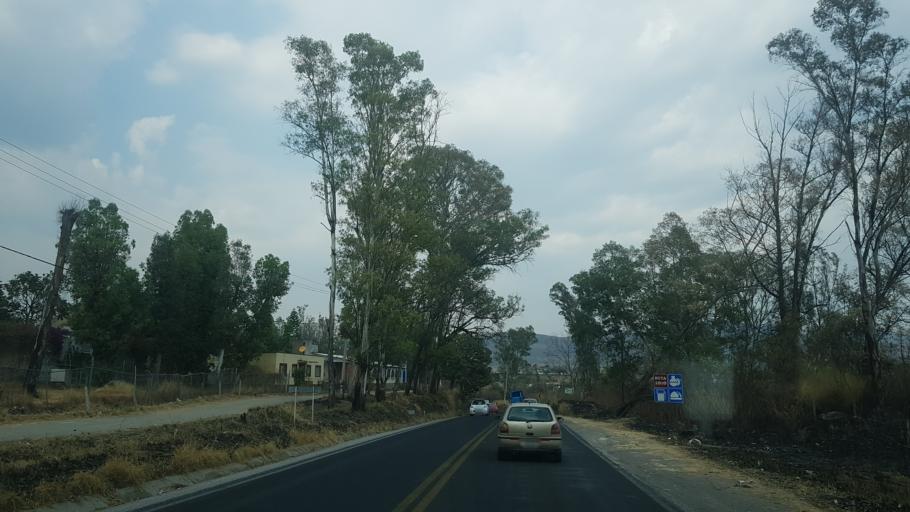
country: MX
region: Puebla
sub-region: Santa Isabel Cholula
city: Santa Ana Acozautla
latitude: 18.9454
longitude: -98.3905
